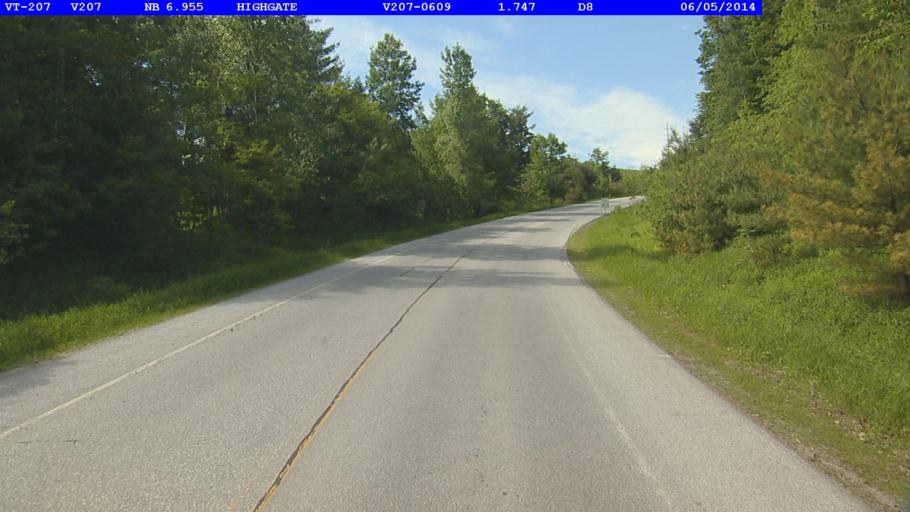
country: US
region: Vermont
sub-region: Franklin County
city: Swanton
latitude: 44.9354
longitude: -73.0499
